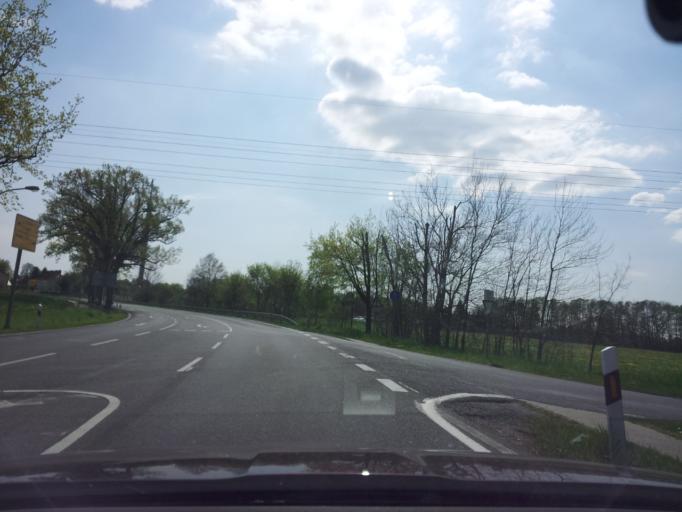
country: DE
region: Brandenburg
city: Treuenbrietzen
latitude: 52.1050
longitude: 12.8813
